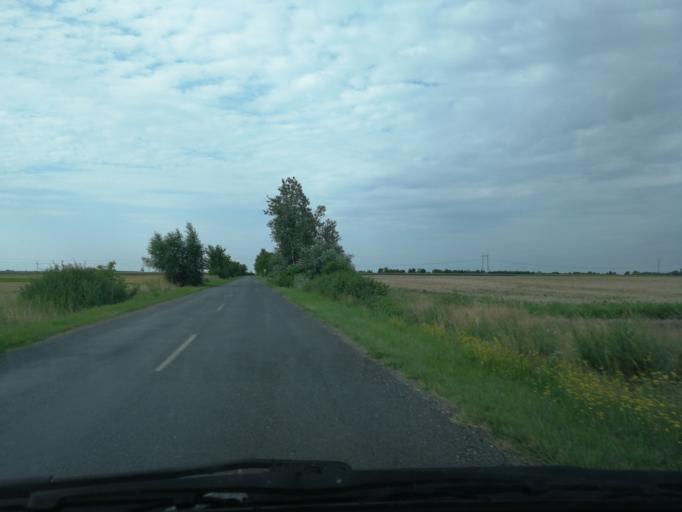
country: HU
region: Bacs-Kiskun
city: Kalocsa
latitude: 46.4804
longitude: 19.0505
